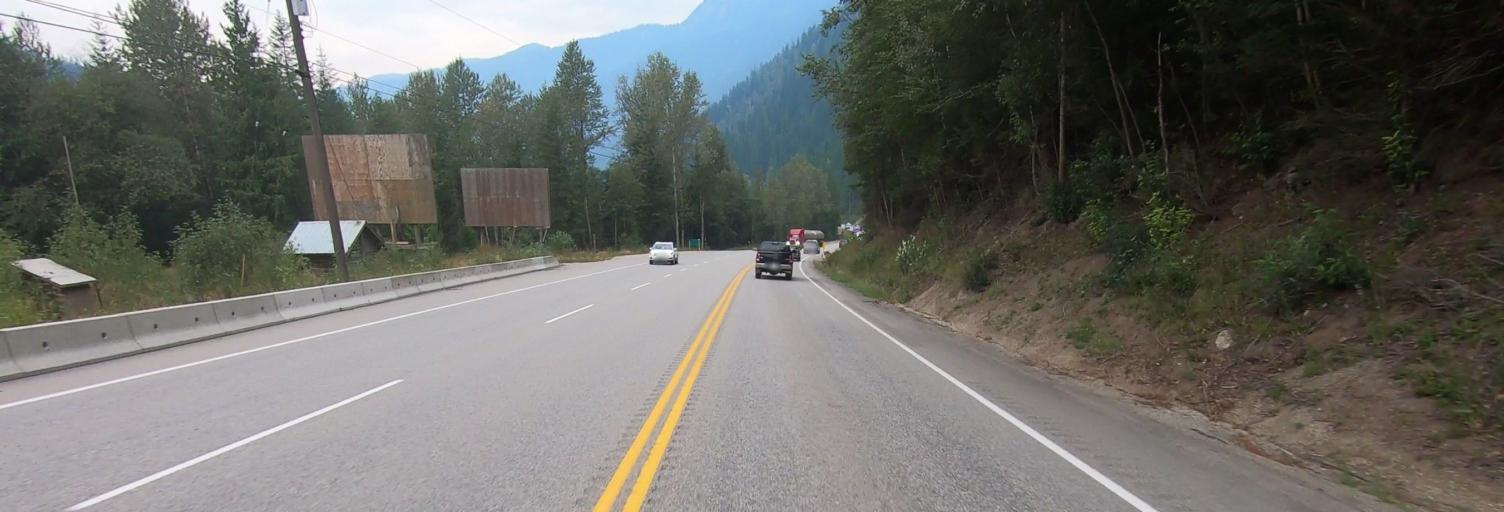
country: CA
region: British Columbia
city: Revelstoke
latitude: 50.9625
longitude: -118.5019
